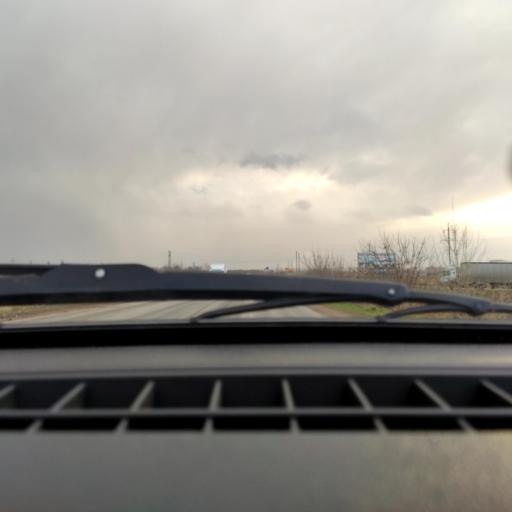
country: RU
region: Bashkortostan
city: Iglino
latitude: 54.7607
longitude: 56.2608
